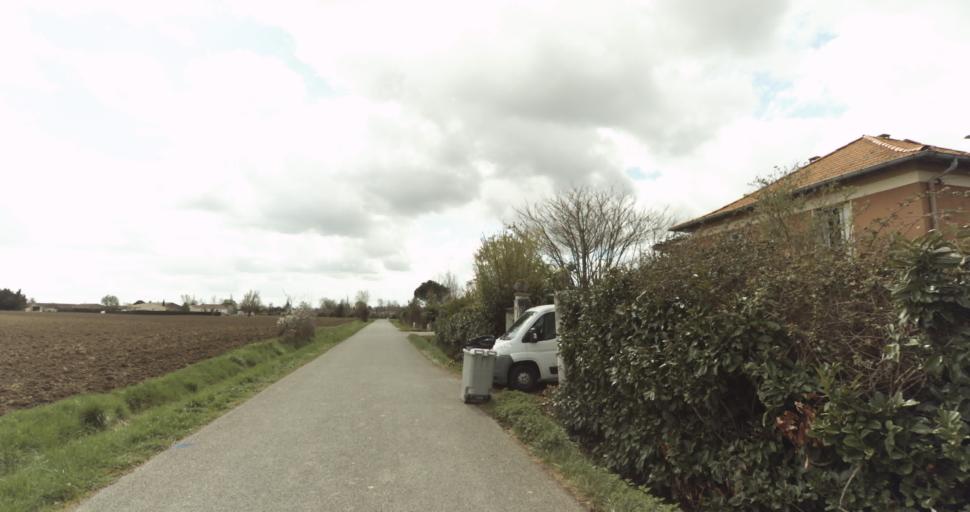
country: FR
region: Midi-Pyrenees
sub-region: Departement de la Haute-Garonne
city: Auterive
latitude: 43.3311
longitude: 1.4698
